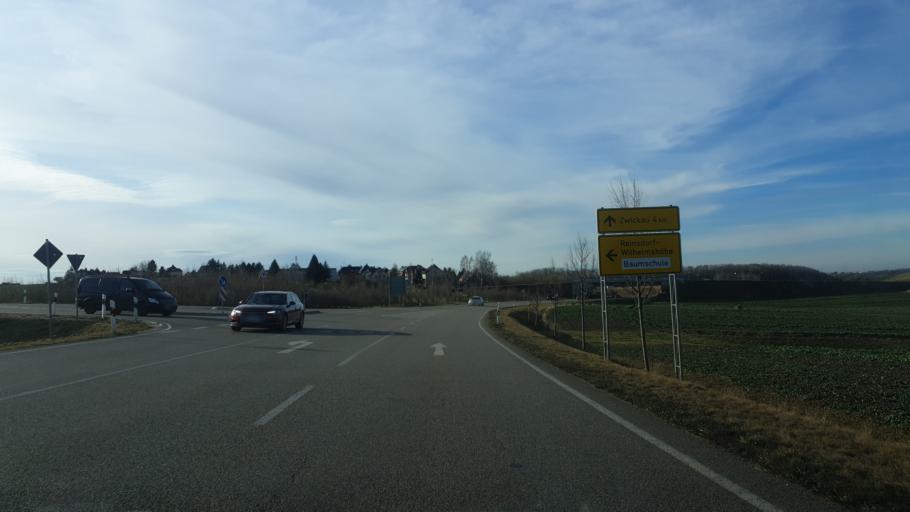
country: DE
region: Saxony
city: Reinsdorf
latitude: 50.6917
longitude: 12.5496
